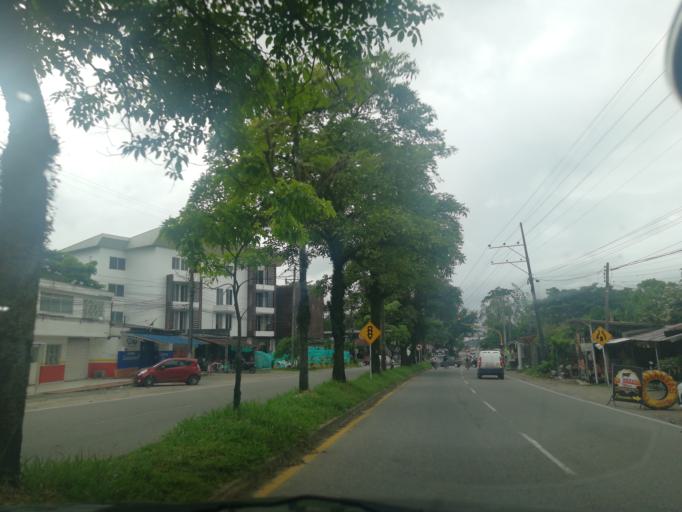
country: CO
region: Meta
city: Acacias
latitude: 3.9892
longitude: -73.7659
